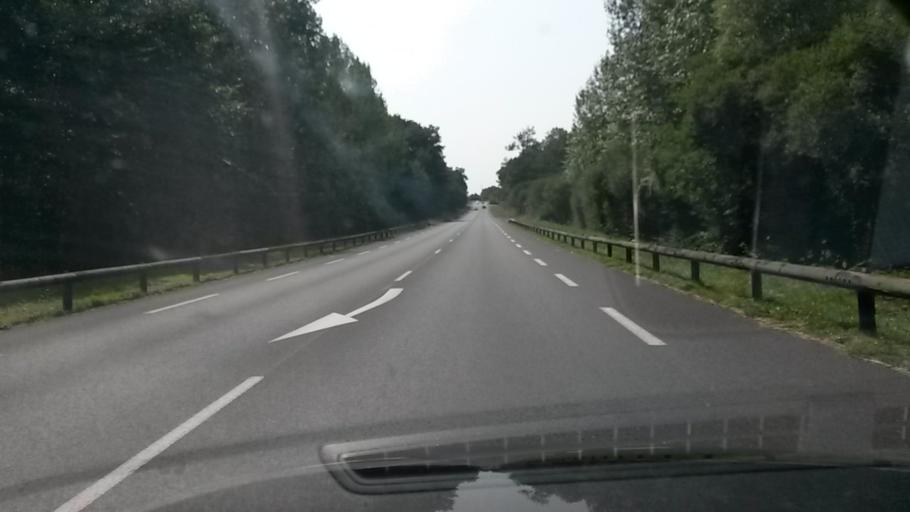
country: FR
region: Pays de la Loire
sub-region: Departement de la Mayenne
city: Chemaze
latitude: 47.7979
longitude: -0.7566
